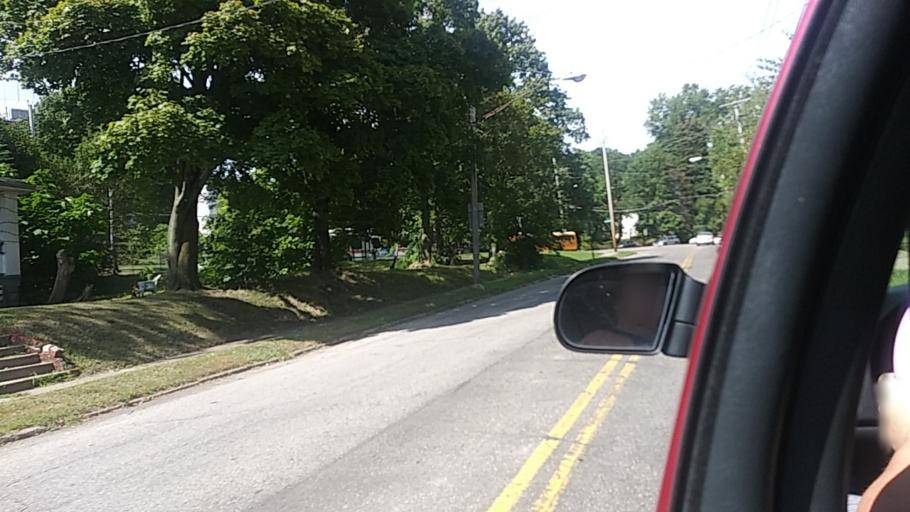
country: US
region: Ohio
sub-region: Summit County
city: Akron
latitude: 41.0670
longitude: -81.5501
